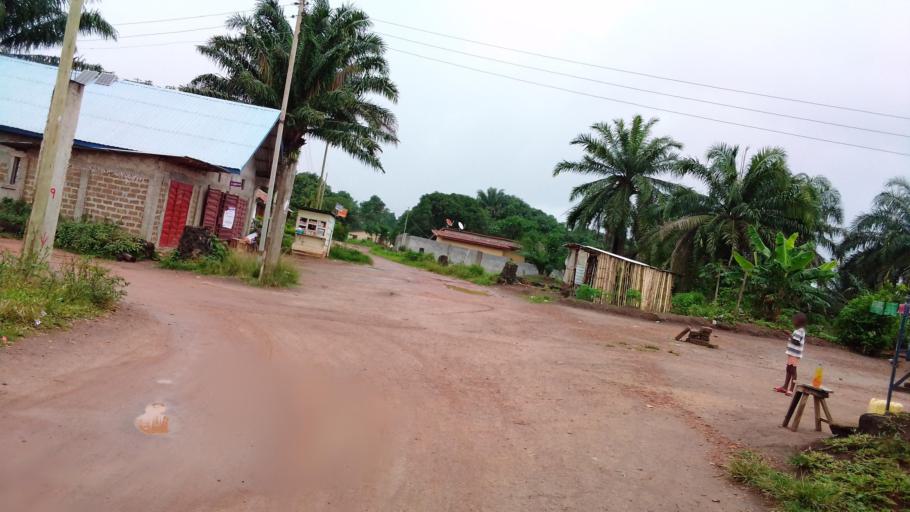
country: SL
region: Eastern Province
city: Kenema
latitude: 7.8667
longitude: -11.1727
